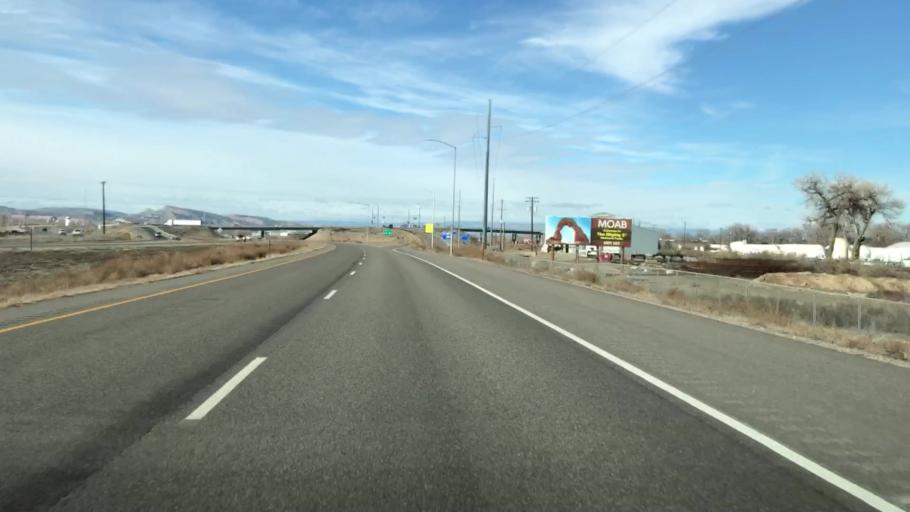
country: US
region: Colorado
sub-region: Mesa County
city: Fruita
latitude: 39.1492
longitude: -108.7345
